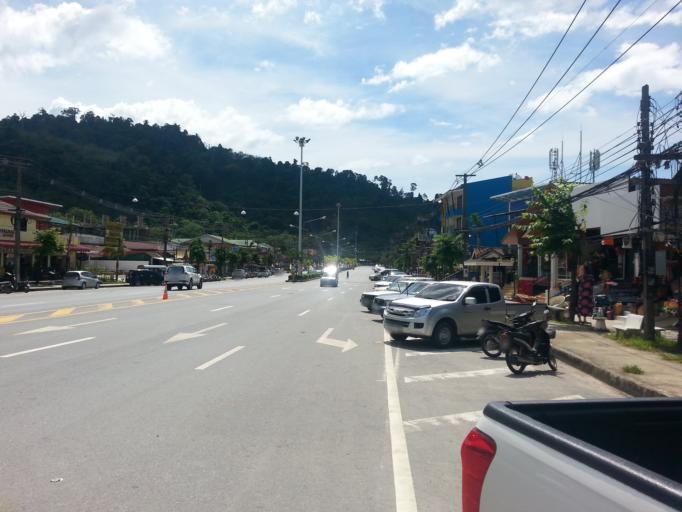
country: TH
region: Phangnga
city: Ban Khao Lak
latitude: 8.6443
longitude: 98.2513
